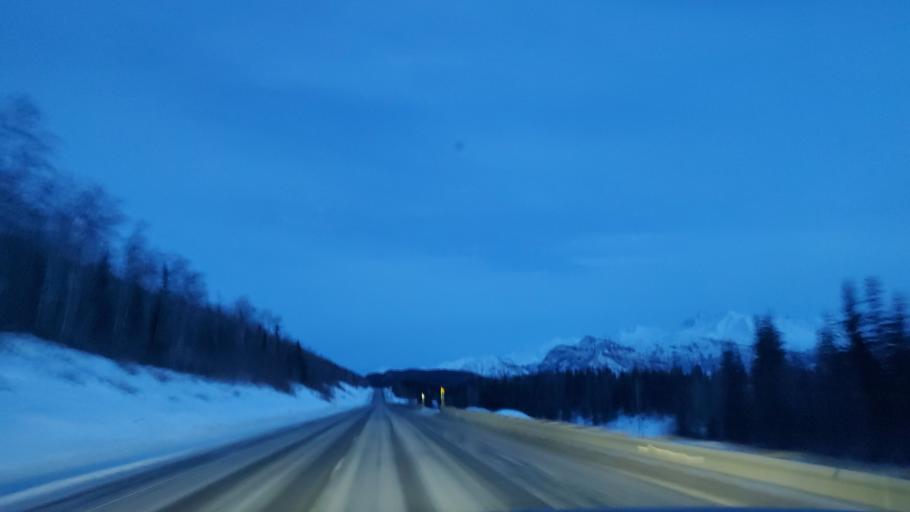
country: US
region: Alaska
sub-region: Matanuska-Susitna Borough
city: Sutton-Alpine
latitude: 61.7972
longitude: -147.7677
